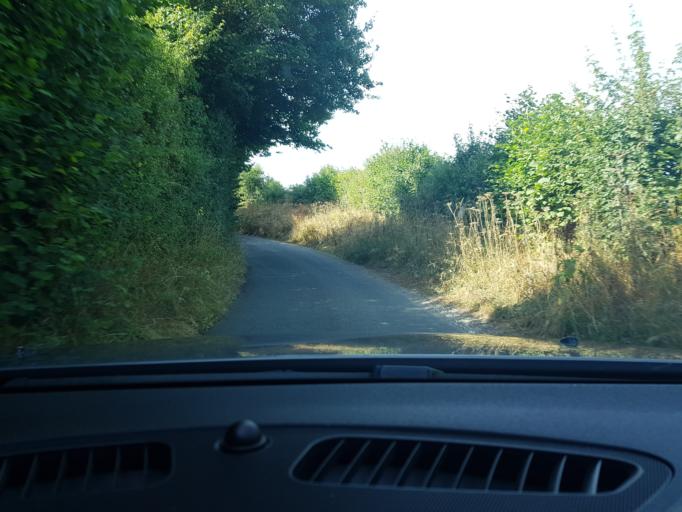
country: GB
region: England
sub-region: West Berkshire
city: Hungerford
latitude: 51.4412
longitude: -1.5057
